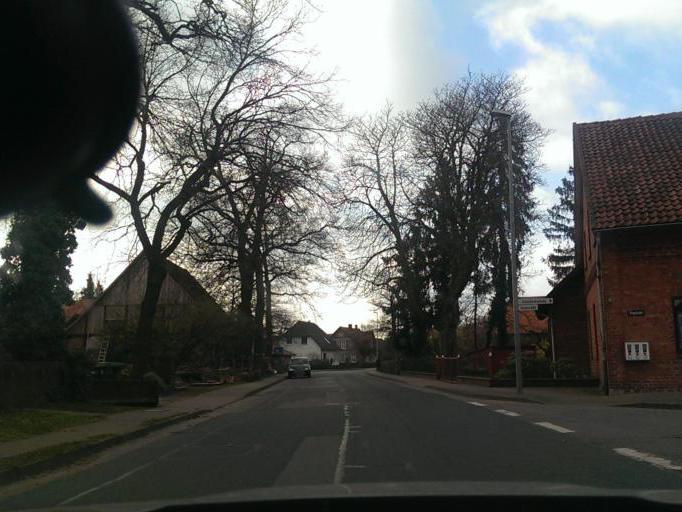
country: DE
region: Lower Saxony
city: Elze
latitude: 52.5831
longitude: 9.7374
